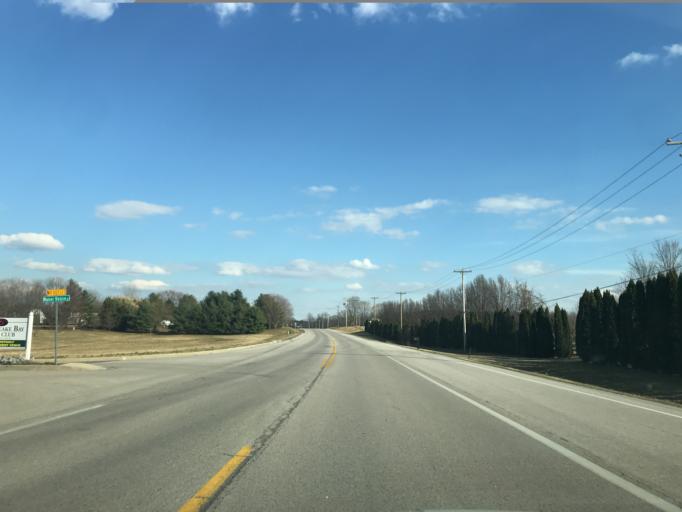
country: US
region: Maryland
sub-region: Cecil County
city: Rising Sun
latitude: 39.6584
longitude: -75.9966
